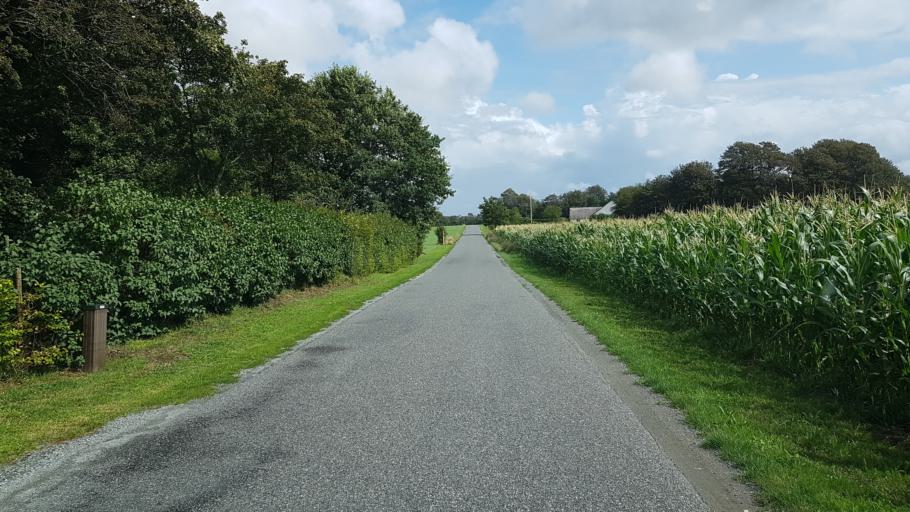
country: DK
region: South Denmark
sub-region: Vejen Kommune
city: Holsted
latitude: 55.4948
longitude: 8.9455
